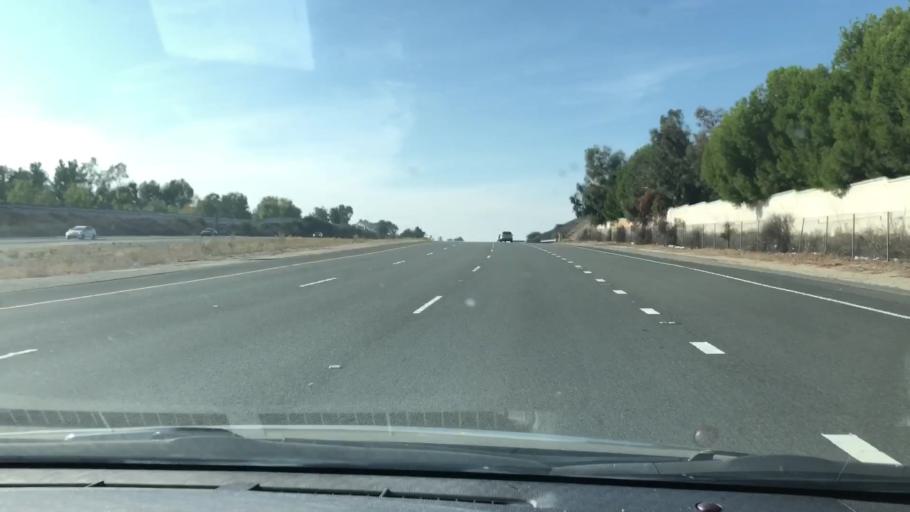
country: US
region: California
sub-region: Orange County
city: Rancho Santa Margarita
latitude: 33.6520
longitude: -117.6127
